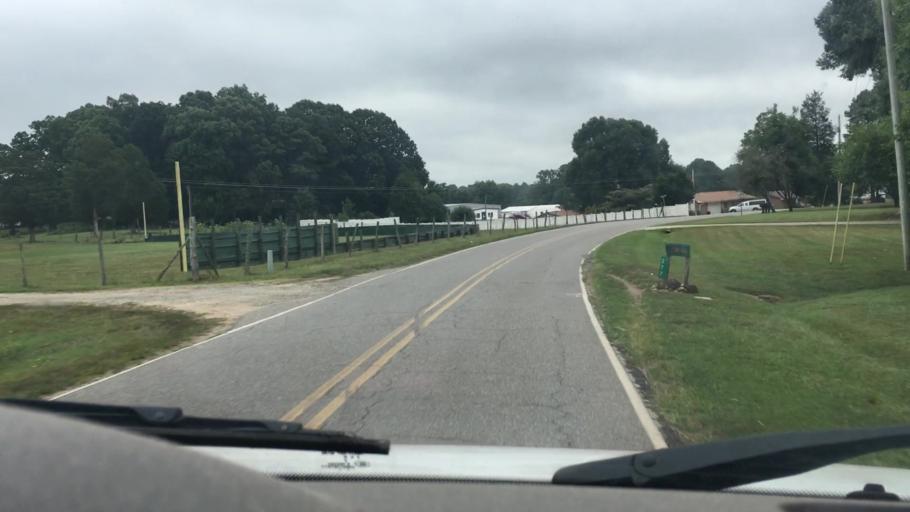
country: US
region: North Carolina
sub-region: Gaston County
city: Davidson
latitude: 35.5301
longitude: -80.8280
